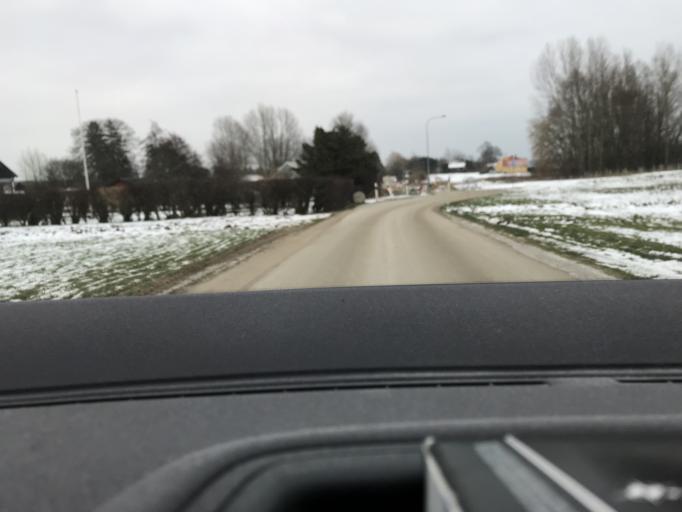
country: SE
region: Skane
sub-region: Ystads Kommun
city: Ystad
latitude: 55.4562
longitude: 13.8550
